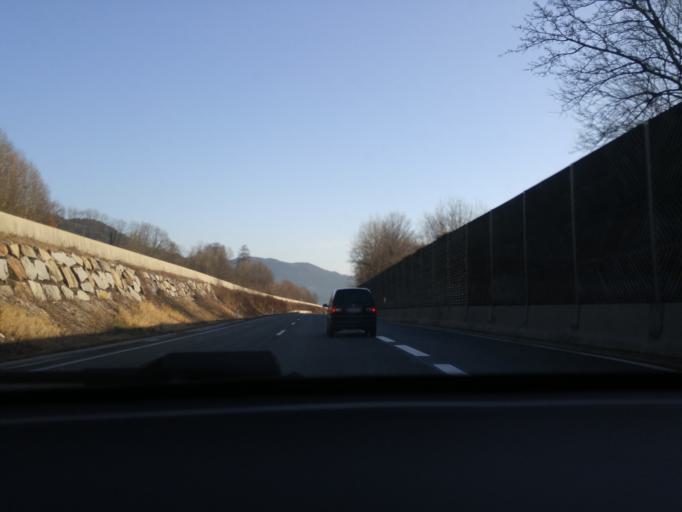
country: AT
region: Upper Austria
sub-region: Politischer Bezirk Vocklabruck
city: Mondsee
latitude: 47.8543
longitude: 13.3590
